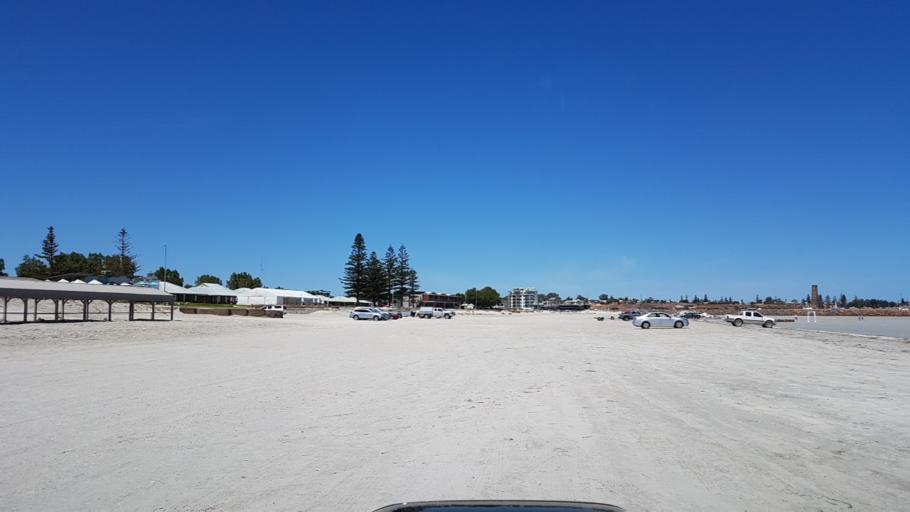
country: AU
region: South Australia
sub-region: Copper Coast
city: Wallaroo
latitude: -33.9176
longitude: 137.6310
